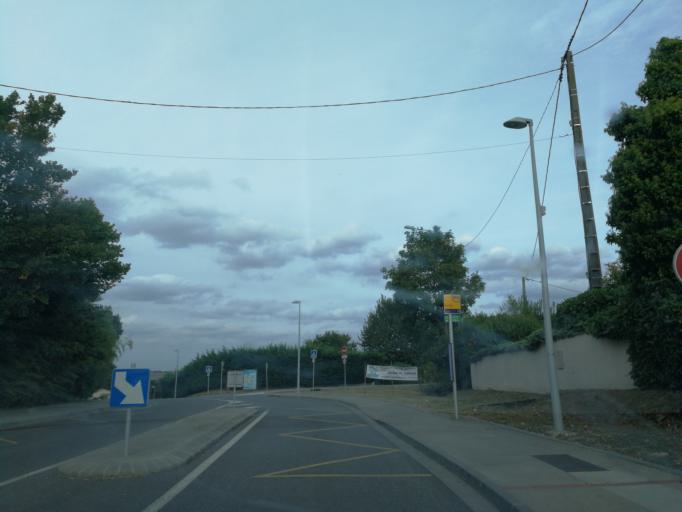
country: FR
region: Midi-Pyrenees
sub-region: Departement de la Haute-Garonne
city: Flourens
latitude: 43.5939
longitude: 1.5574
